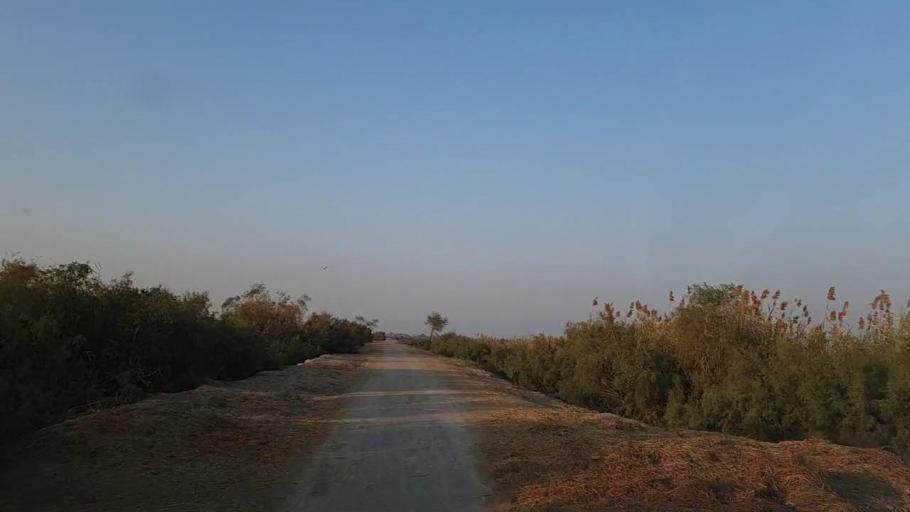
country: PK
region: Sindh
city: Bandhi
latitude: 26.5439
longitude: 68.3166
